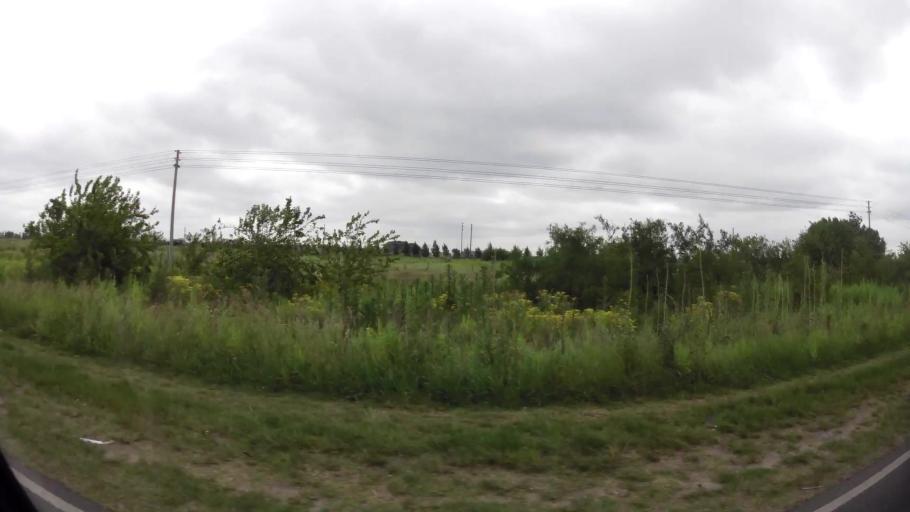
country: AR
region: Buenos Aires
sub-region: Partido de San Vicente
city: San Vicente
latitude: -34.9618
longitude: -58.4656
